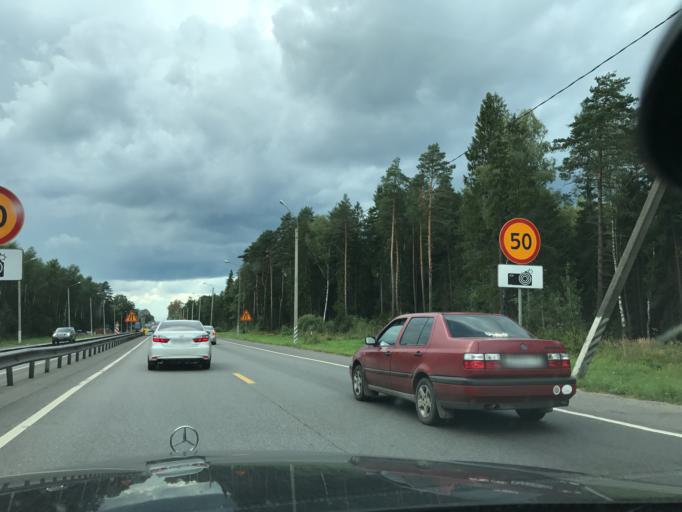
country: RU
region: Vladimir
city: Petushki
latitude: 55.9286
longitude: 39.3288
